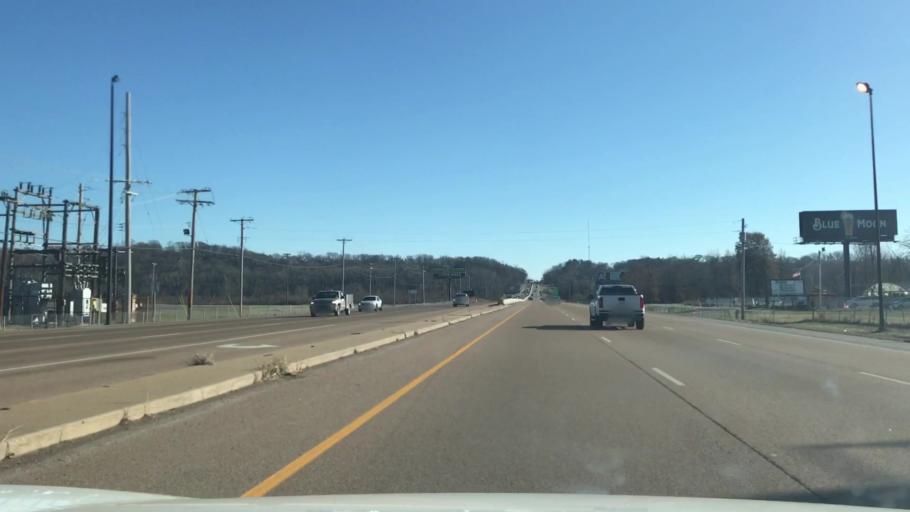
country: US
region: Illinois
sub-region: Saint Clair County
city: Alorton
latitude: 38.5739
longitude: -90.0984
